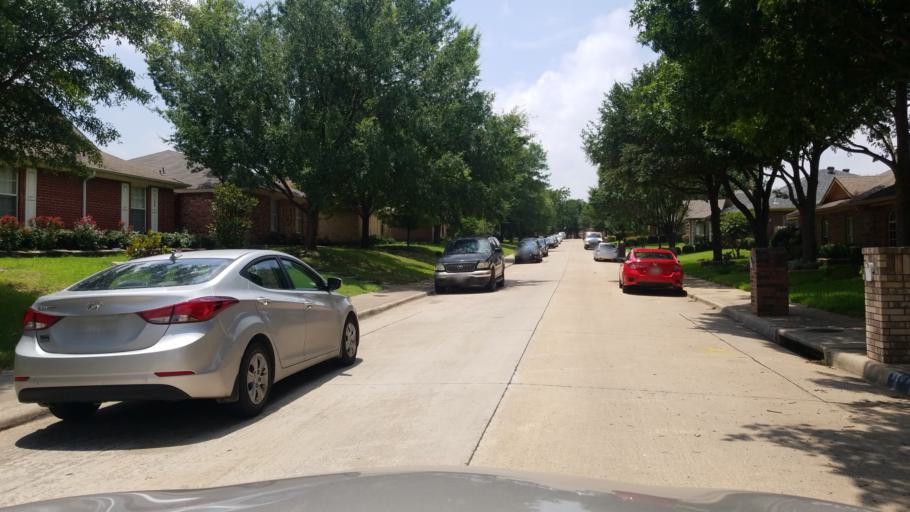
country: US
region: Texas
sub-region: Dallas County
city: Duncanville
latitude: 32.6848
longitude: -96.9102
